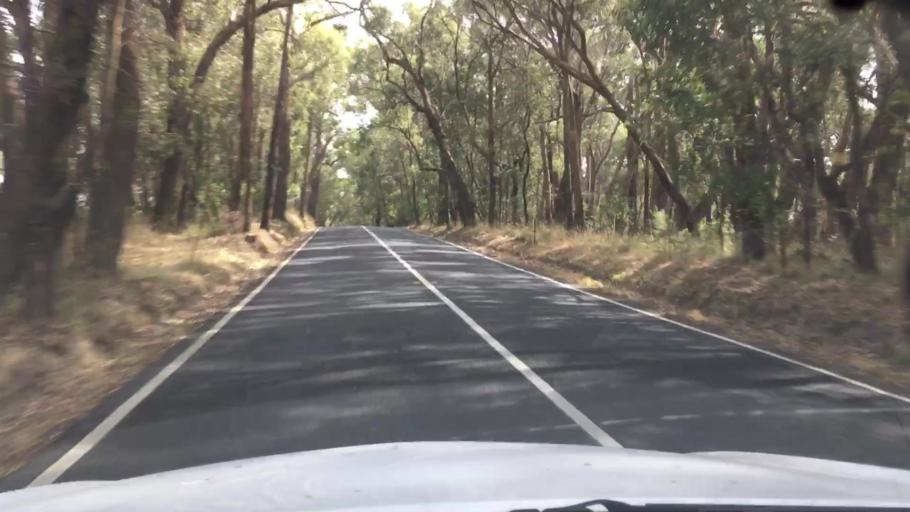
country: AU
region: Victoria
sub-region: Yarra Ranges
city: Macclesfield
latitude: -37.8447
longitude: 145.4853
